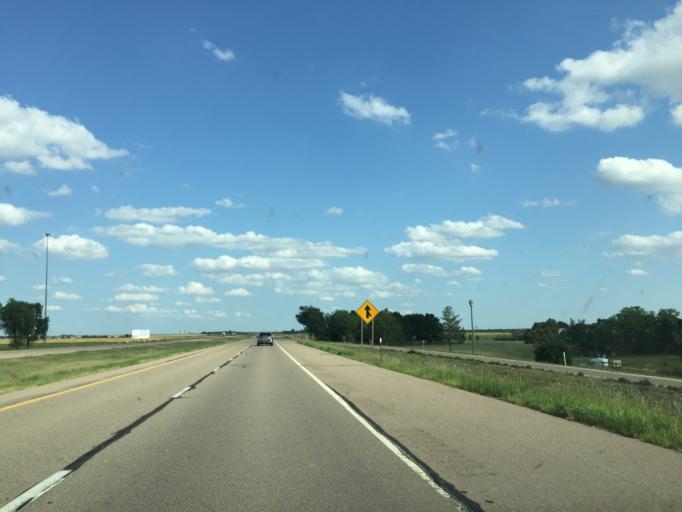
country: US
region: Kansas
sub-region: Gove County
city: Gove
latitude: 39.0573
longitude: -100.2406
